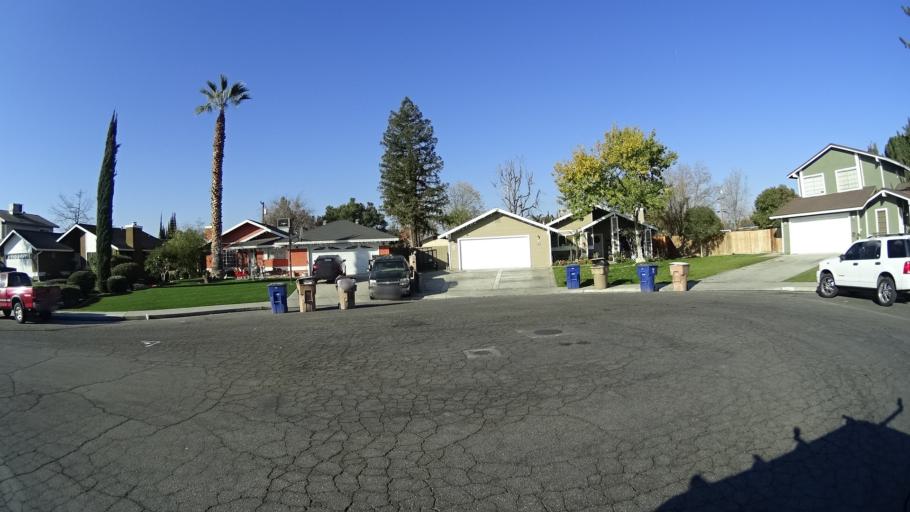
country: US
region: California
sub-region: Kern County
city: Greenfield
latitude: 35.3020
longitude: -119.0157
